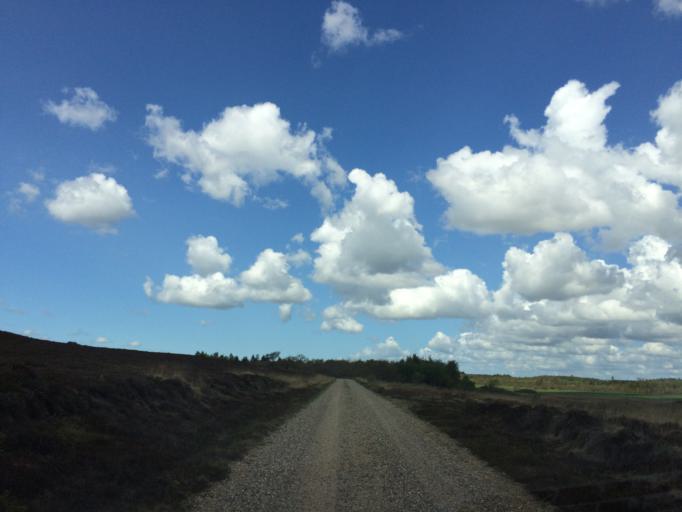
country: DK
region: Central Jutland
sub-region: Holstebro Kommune
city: Ulfborg
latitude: 56.2833
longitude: 8.4627
